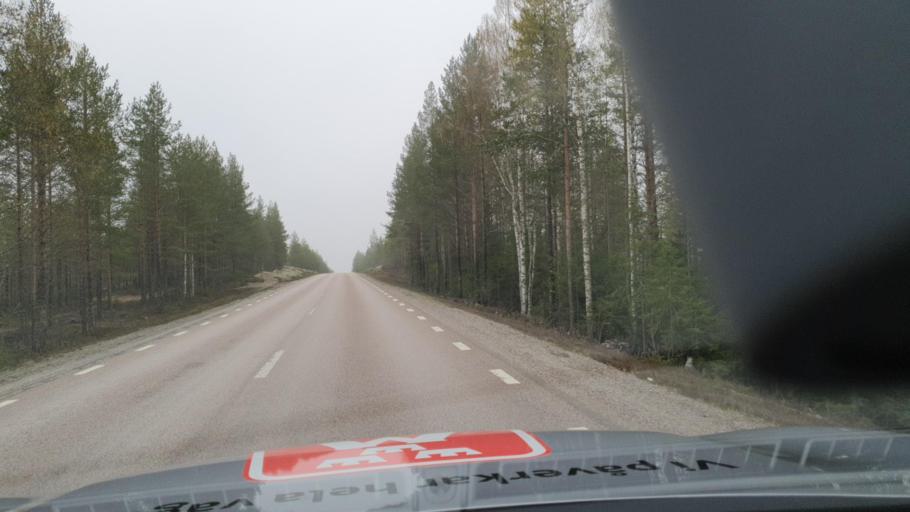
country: SE
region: Vaesternorrland
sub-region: OErnskoeldsviks Kommun
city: Husum
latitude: 63.4398
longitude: 18.9557
